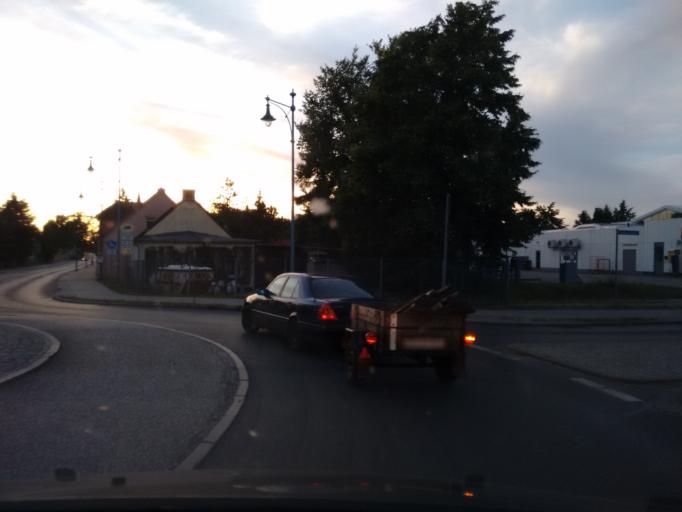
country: DE
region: Brandenburg
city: Beeskow
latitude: 52.1674
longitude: 14.2592
